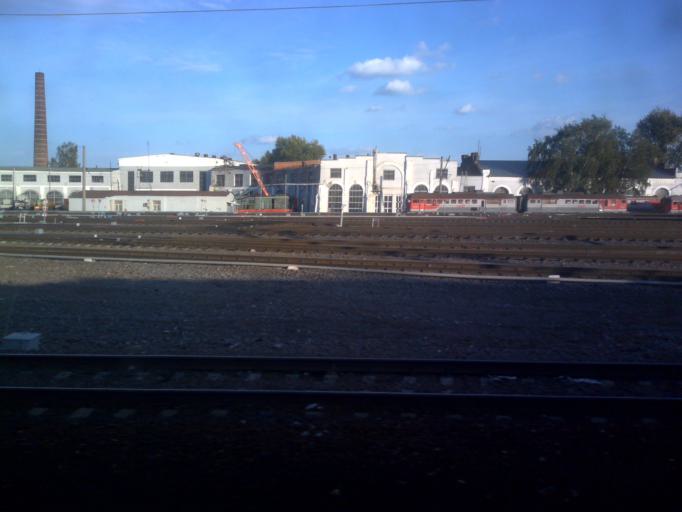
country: RU
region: Moscow
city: Mar'ino
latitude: 55.6713
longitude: 37.7265
